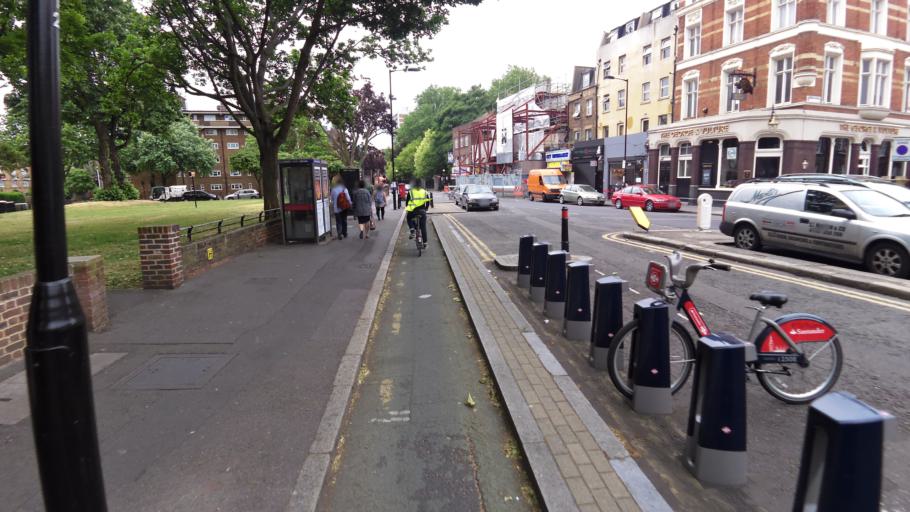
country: GB
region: England
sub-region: Greater London
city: Barbican
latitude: 51.5294
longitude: -0.0833
